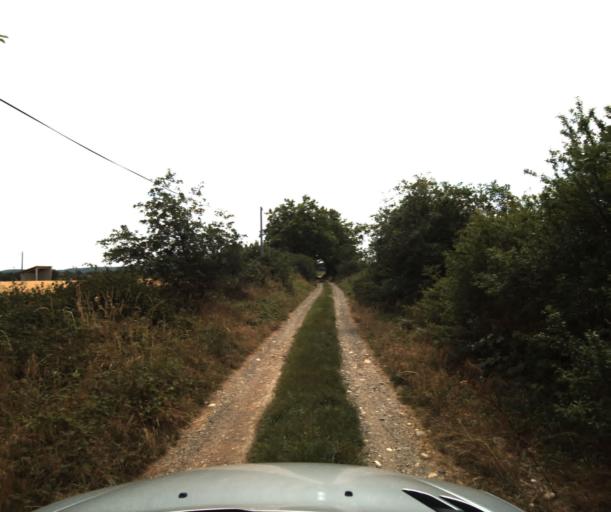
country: FR
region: Midi-Pyrenees
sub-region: Departement de la Haute-Garonne
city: Lacasse
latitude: 43.4120
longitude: 1.2686
